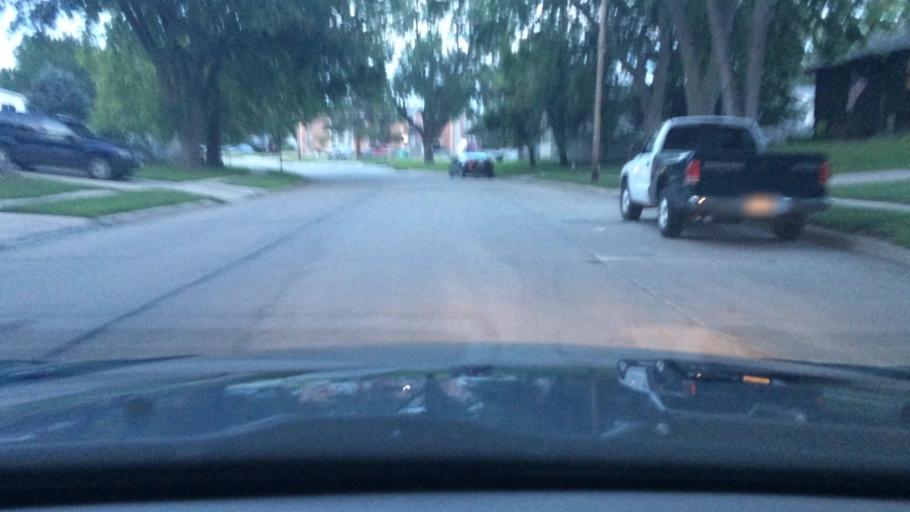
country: US
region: Nebraska
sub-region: Sarpy County
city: La Vista
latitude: 41.1850
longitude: -96.0485
